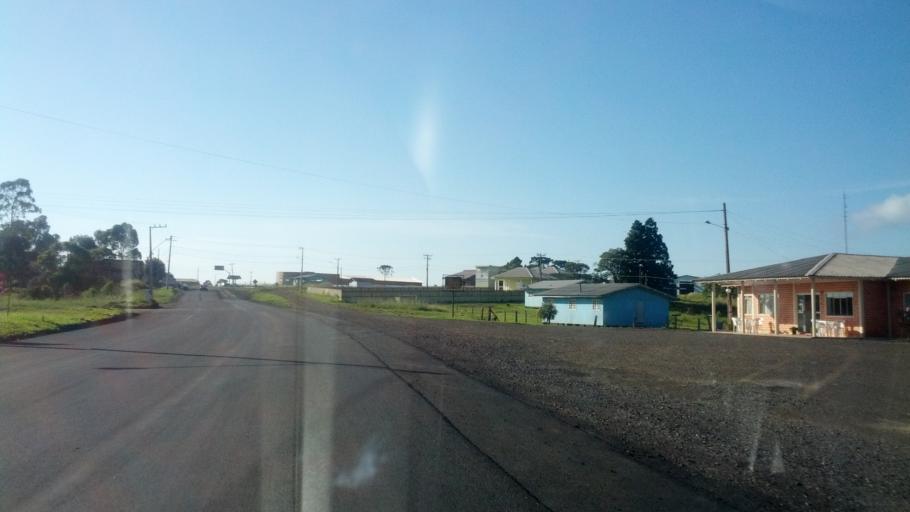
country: BR
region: Santa Catarina
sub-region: Lages
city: Lages
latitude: -27.9416
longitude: -50.5098
